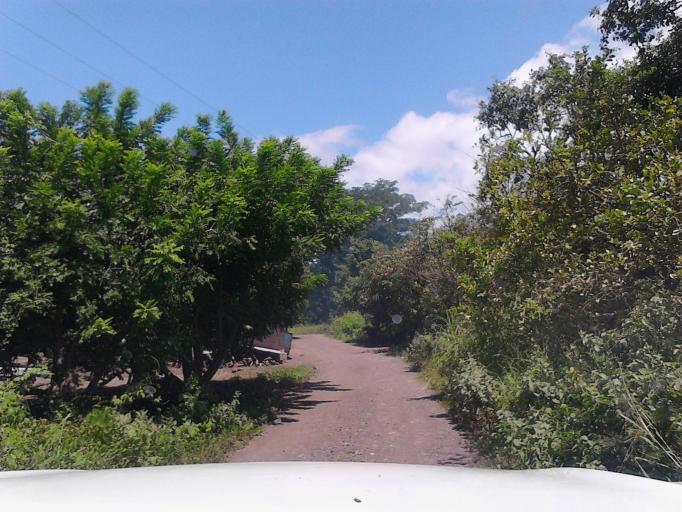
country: NI
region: Matagalpa
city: Ciudad Dario
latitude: 12.8955
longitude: -86.1433
